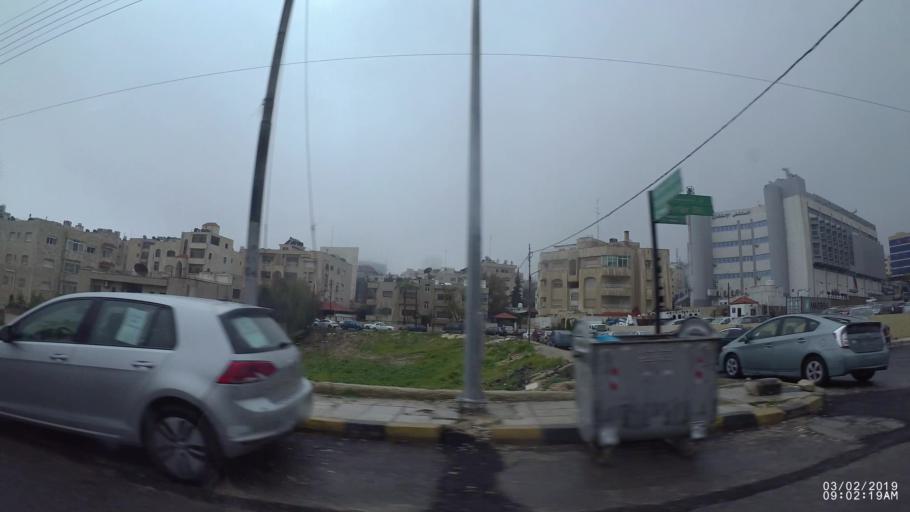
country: JO
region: Amman
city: Amman
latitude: 31.9651
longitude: 35.8877
